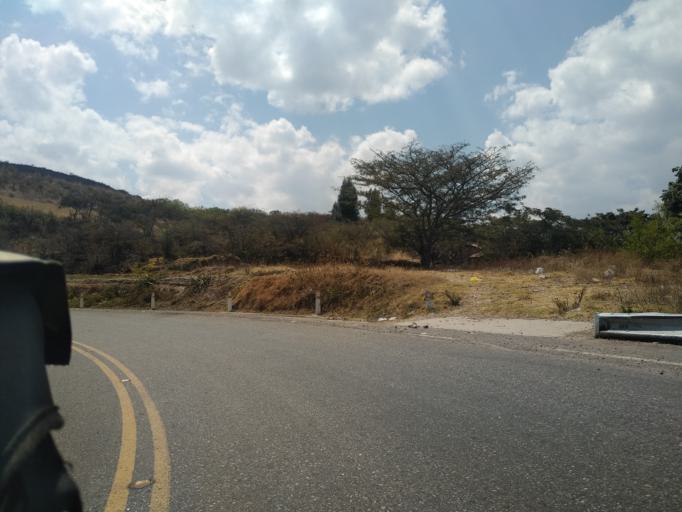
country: PE
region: Cajamarca
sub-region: Provincia de Cajabamba
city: Cauday
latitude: -7.6143
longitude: -78.0855
